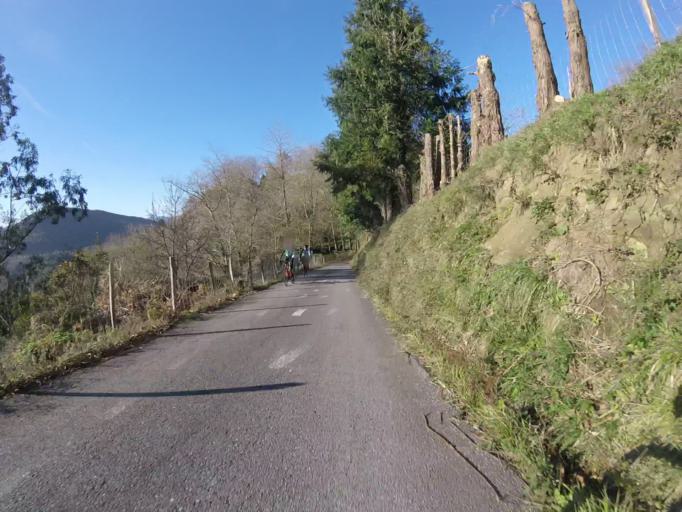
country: ES
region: Basque Country
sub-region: Provincia de Guipuzcoa
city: Usurbil
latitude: 43.3031
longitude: -2.0475
